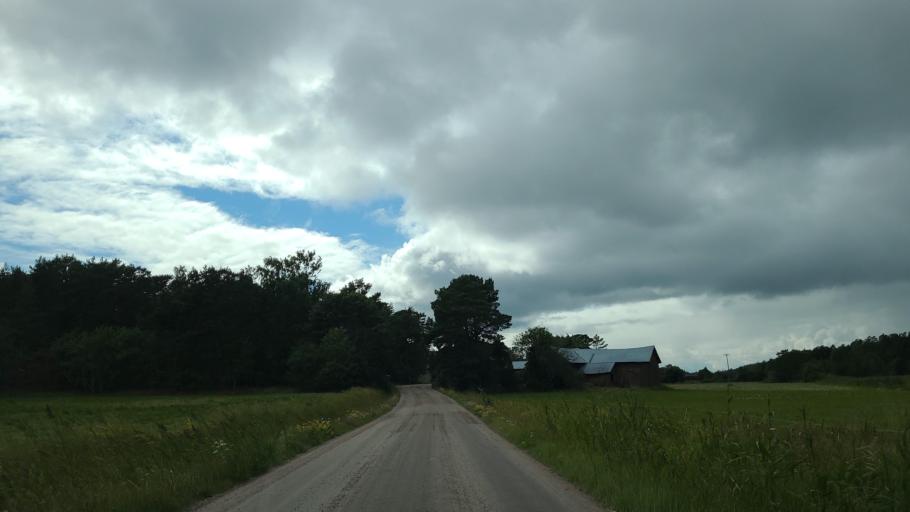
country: FI
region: Varsinais-Suomi
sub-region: Aboland-Turunmaa
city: Nagu
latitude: 60.2028
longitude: 21.8796
